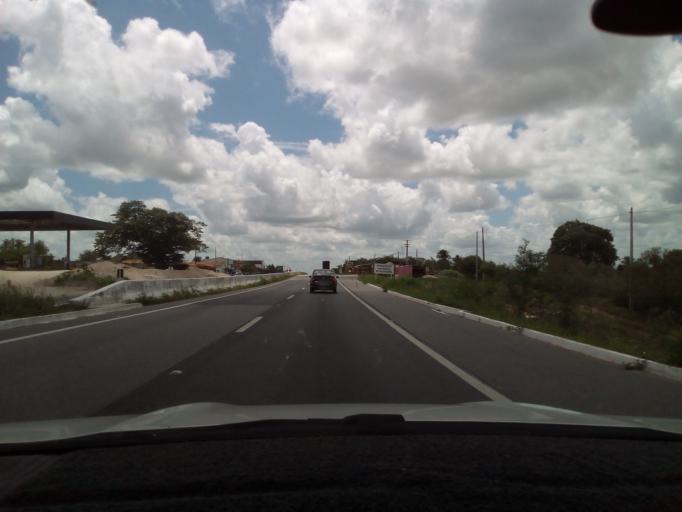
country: BR
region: Paraiba
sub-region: Gurinhem
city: Gurinhem
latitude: -7.1735
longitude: -35.3958
